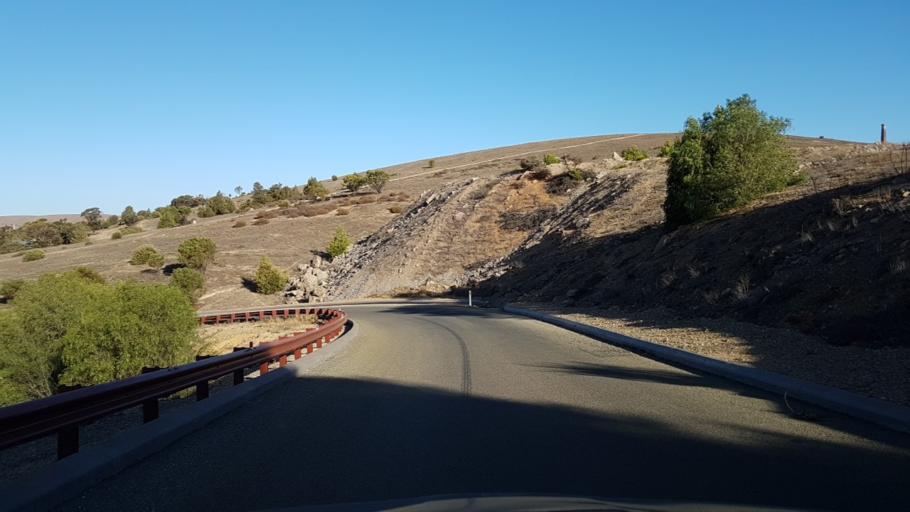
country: AU
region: South Australia
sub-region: Clare and Gilbert Valleys
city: Clare
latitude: -33.6767
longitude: 138.9293
